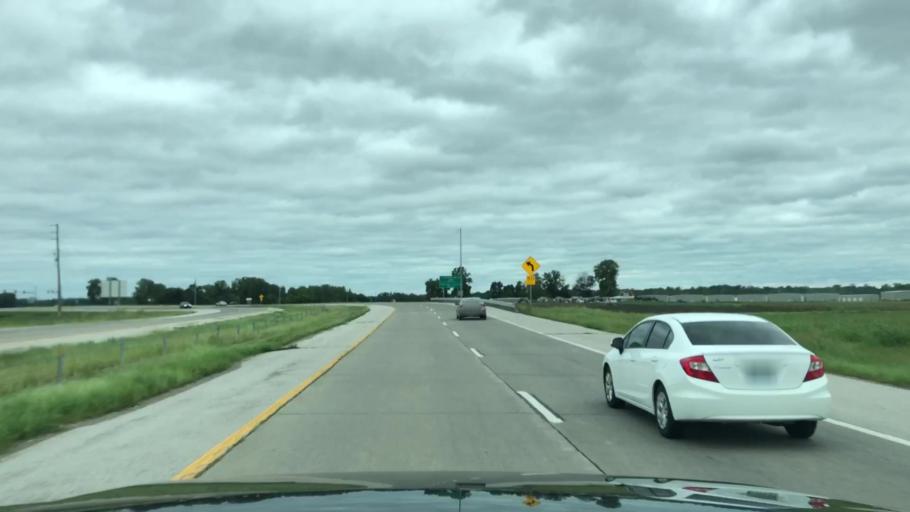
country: US
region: Missouri
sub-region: Saint Charles County
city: Saint Charles
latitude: 38.7278
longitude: -90.4966
